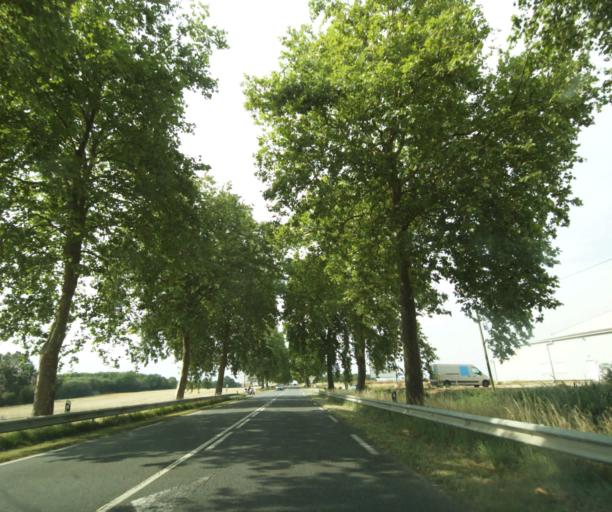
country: FR
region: Centre
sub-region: Departement d'Indre-et-Loire
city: Saint-Paterne-Racan
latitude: 47.6165
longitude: 0.5063
